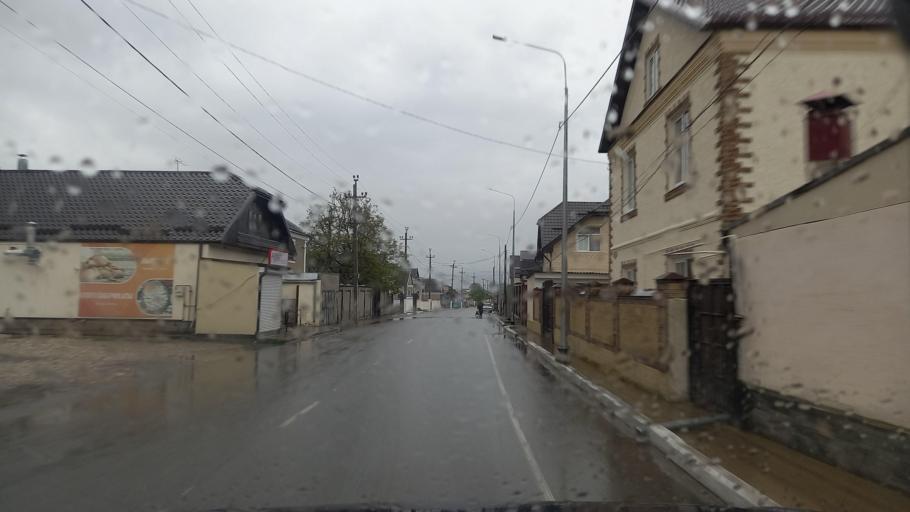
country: RU
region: Kabardino-Balkariya
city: Gundelen
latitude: 43.5959
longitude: 43.1639
